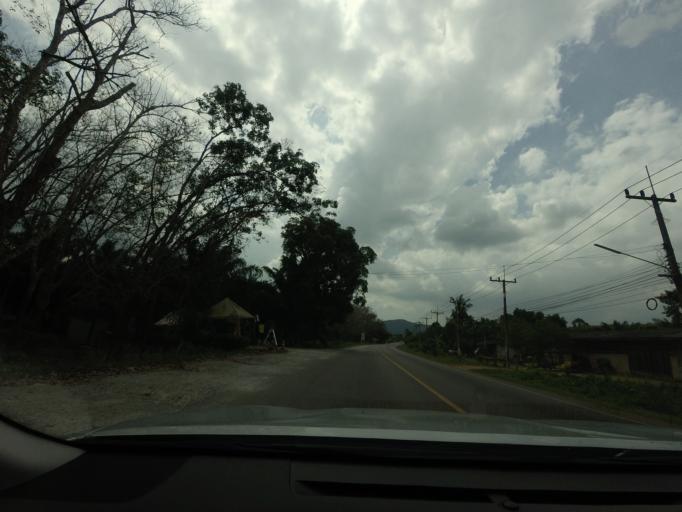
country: TH
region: Phangnga
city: Ban Ao Nang
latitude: 8.1254
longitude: 98.8054
